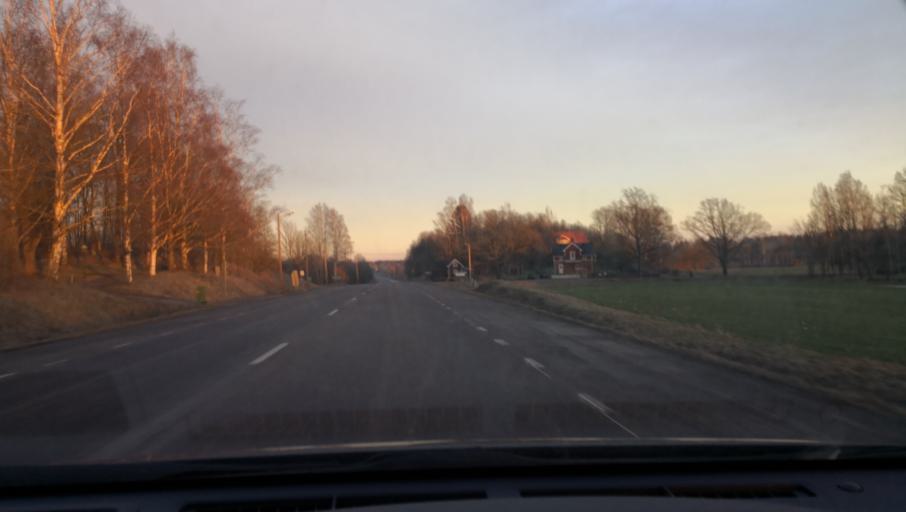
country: SE
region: OErebro
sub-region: Orebro Kommun
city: Vintrosa
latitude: 59.2431
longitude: 14.9932
